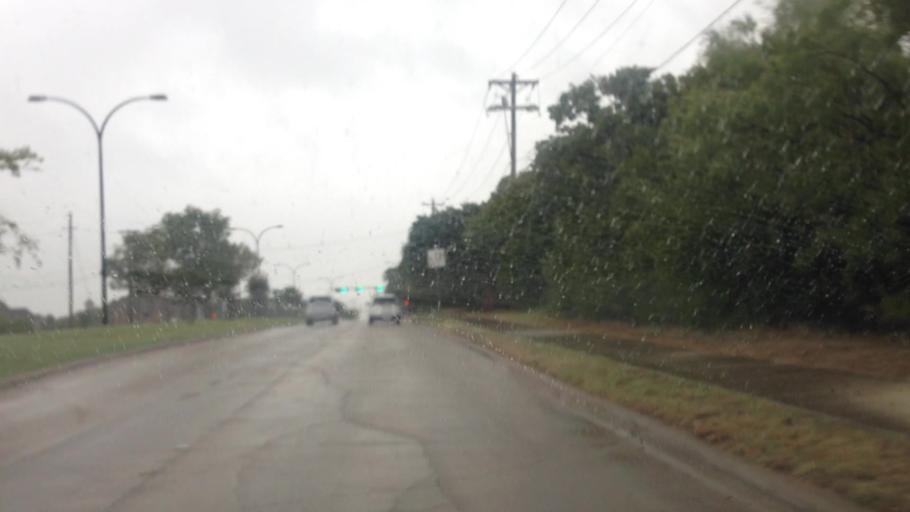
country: US
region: Texas
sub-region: Tarrant County
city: Keller
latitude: 32.9103
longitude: -97.2322
